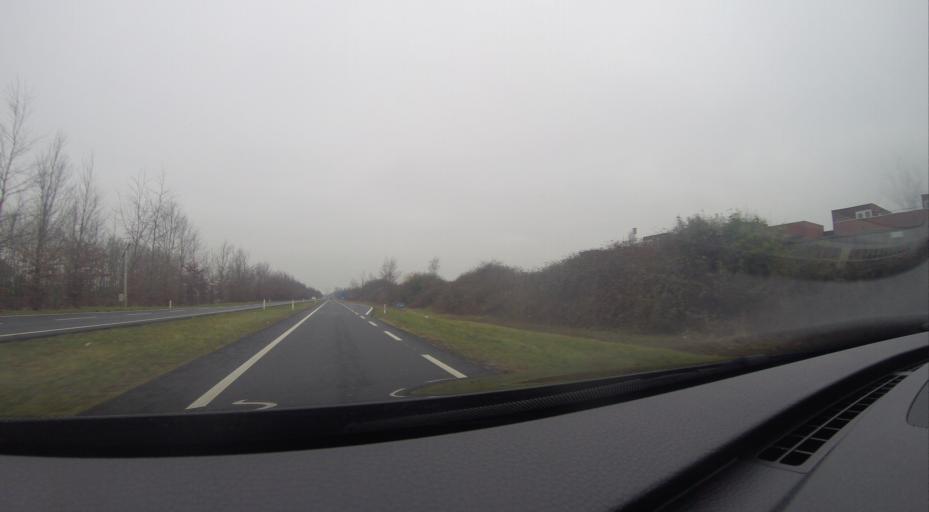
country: NL
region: Gelderland
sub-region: Gemeente Zutphen
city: Leesten
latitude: 52.1234
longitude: 6.2350
